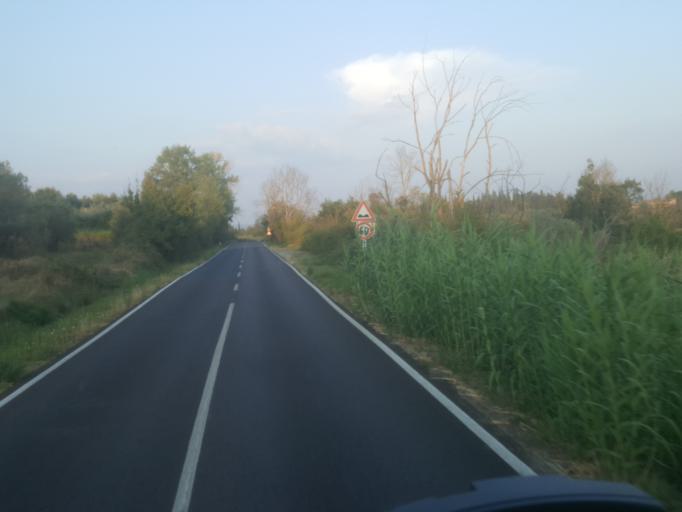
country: IT
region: Tuscany
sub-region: Province of Florence
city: Certaldo
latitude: 43.5440
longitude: 10.9983
